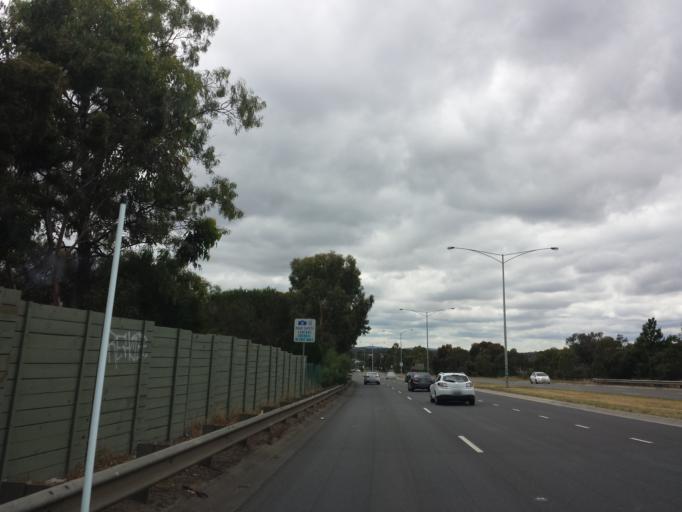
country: AU
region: Victoria
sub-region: Banyule
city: Watsonia North
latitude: -37.7066
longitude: 145.0880
